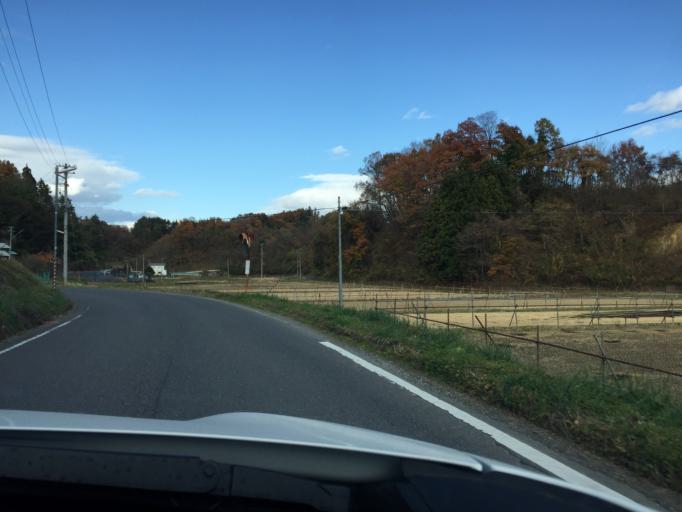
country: JP
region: Fukushima
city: Miharu
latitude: 37.3816
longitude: 140.5285
